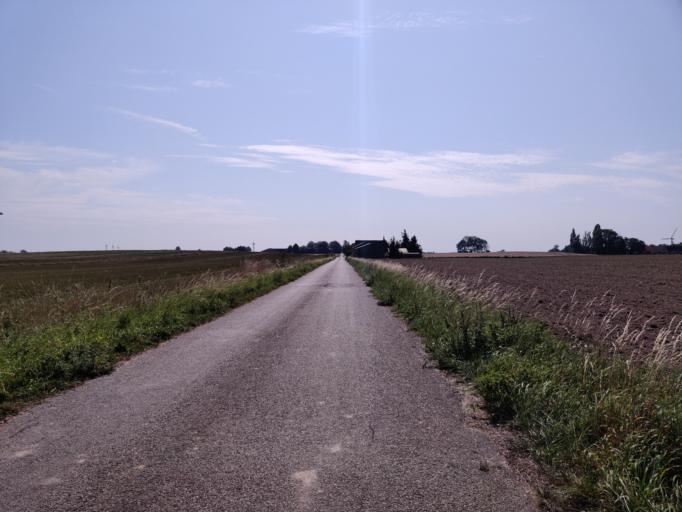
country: DK
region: Zealand
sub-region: Guldborgsund Kommune
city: Nykobing Falster
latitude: 54.6838
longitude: 11.8916
